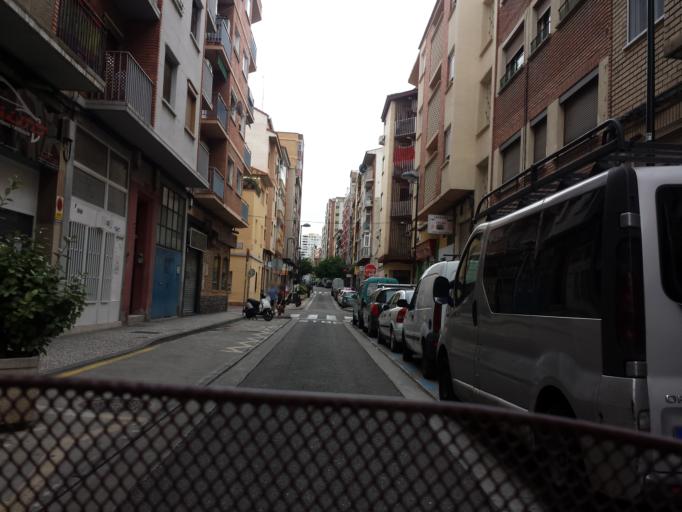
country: ES
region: Aragon
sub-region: Provincia de Zaragoza
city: Delicias
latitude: 41.6517
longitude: -0.9005
